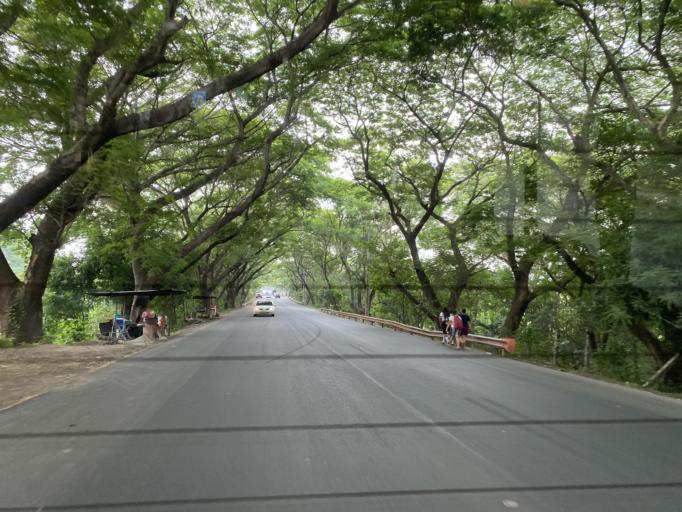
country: SV
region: San Miguel
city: Chirilagua
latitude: 13.3525
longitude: -88.1477
